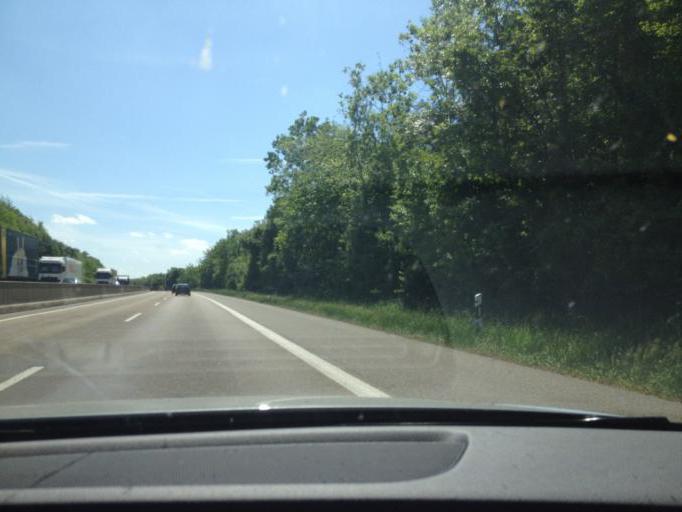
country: DE
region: North Rhine-Westphalia
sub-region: Regierungsbezirk Koln
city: Euskirchen
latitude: 50.6338
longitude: 6.7186
